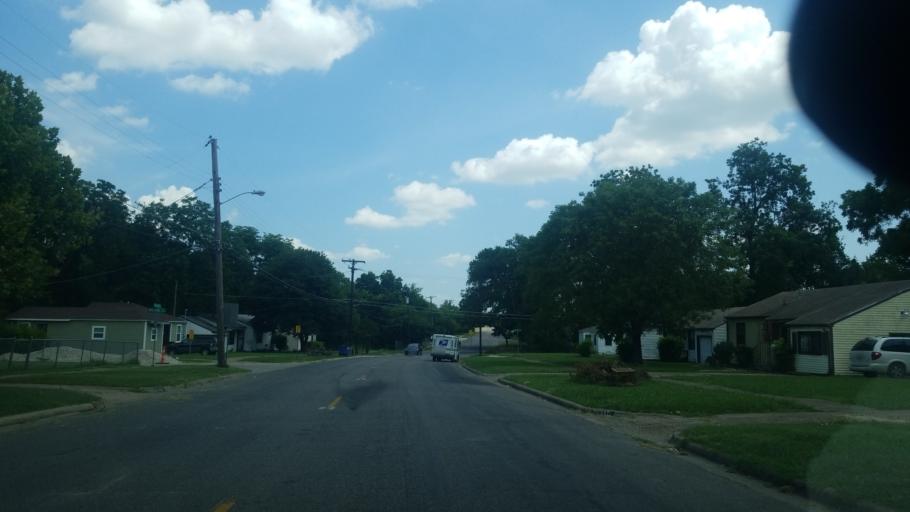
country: US
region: Texas
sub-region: Dallas County
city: Dallas
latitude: 32.7148
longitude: -96.7864
